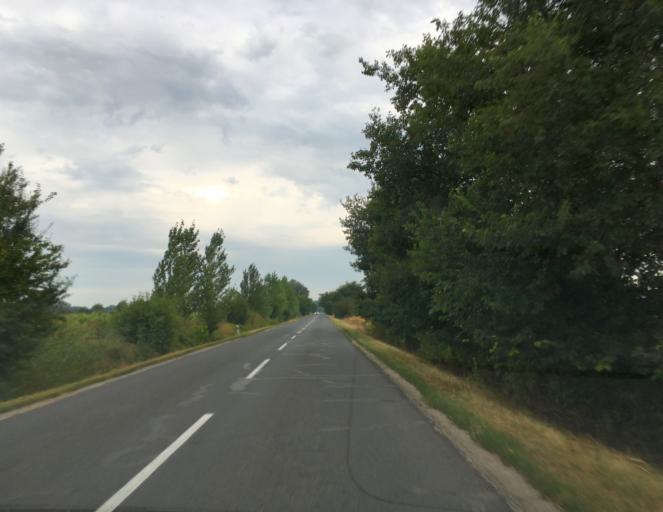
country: SK
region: Trnavsky
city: Gabcikovo
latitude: 47.8943
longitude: 17.6740
